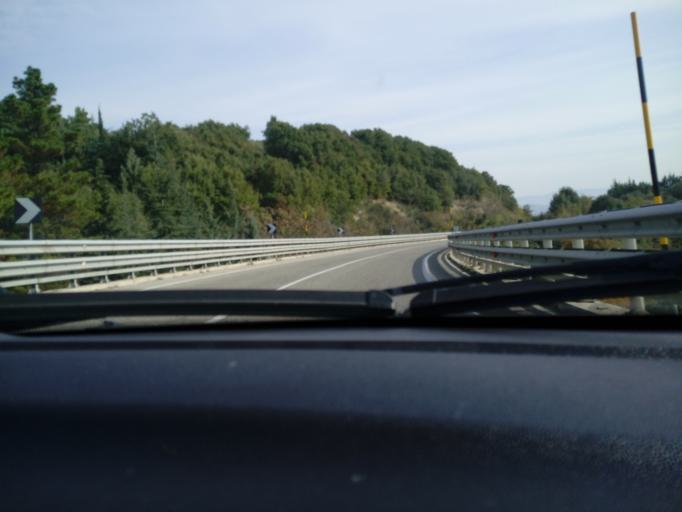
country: IT
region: Molise
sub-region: Provincia di Campobasso
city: Riccia
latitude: 41.5123
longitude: 14.8427
